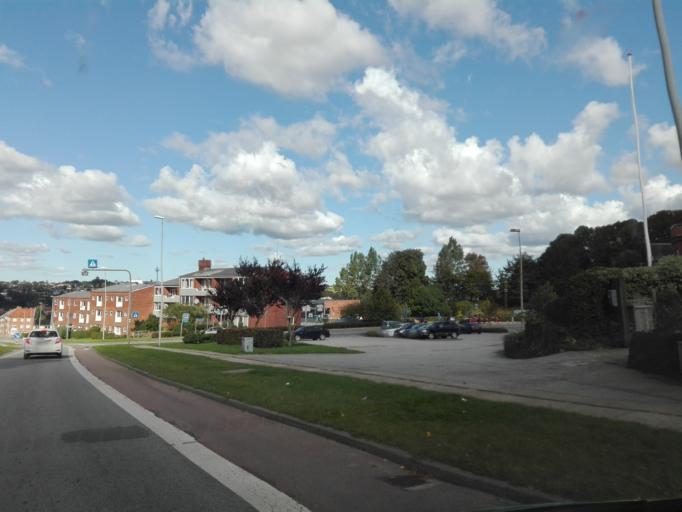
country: DK
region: North Denmark
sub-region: Mariagerfjord Kommune
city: Hobro
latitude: 56.6330
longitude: 9.8003
